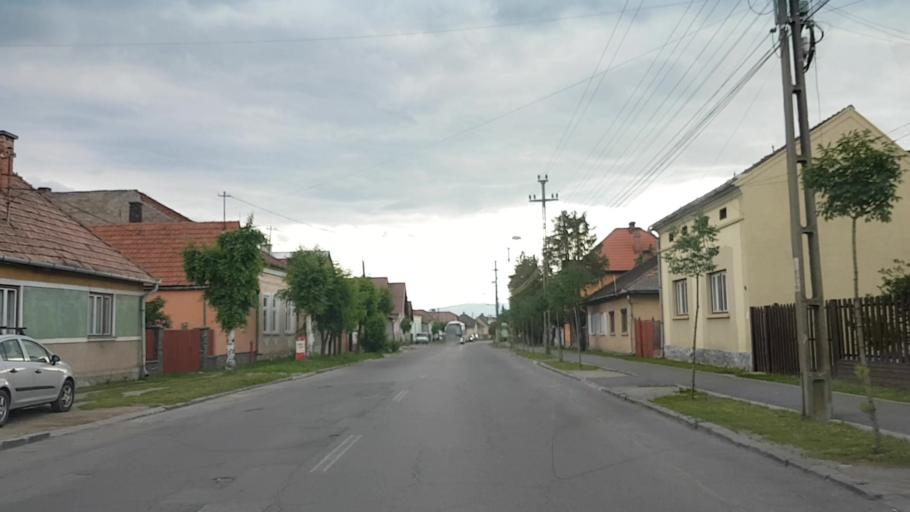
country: RO
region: Harghita
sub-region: Municipiul Gheorgheni
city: Gheorgheni
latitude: 46.7175
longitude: 25.5874
